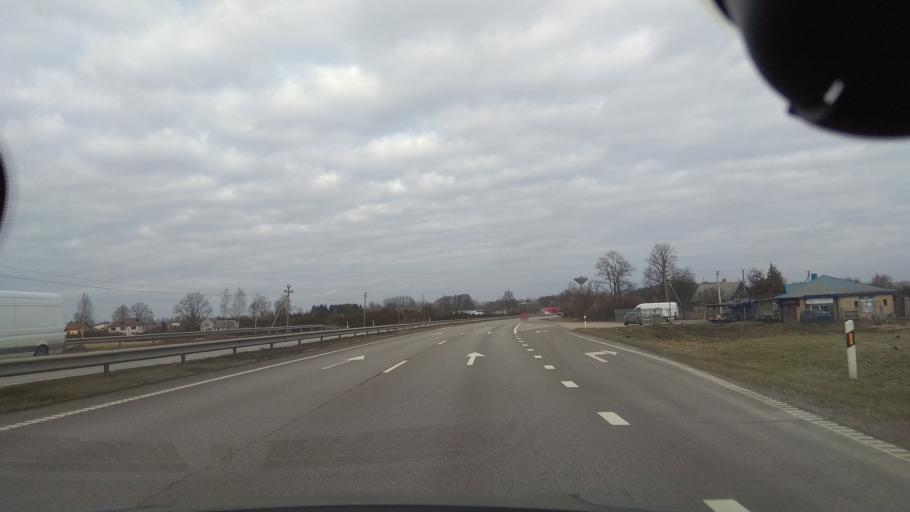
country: LT
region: Kauno apskritis
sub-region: Kauno rajonas
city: Akademija (Kaunas)
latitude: 54.8838
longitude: 23.8191
